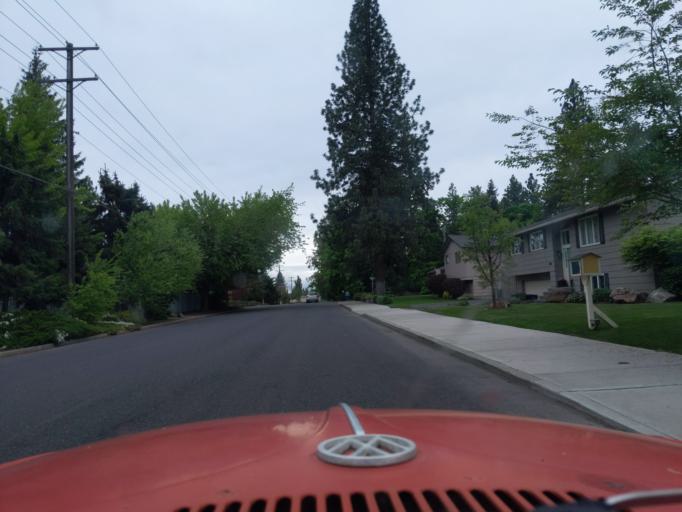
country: US
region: Washington
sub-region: Spokane County
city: Spokane
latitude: 47.6162
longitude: -117.3793
